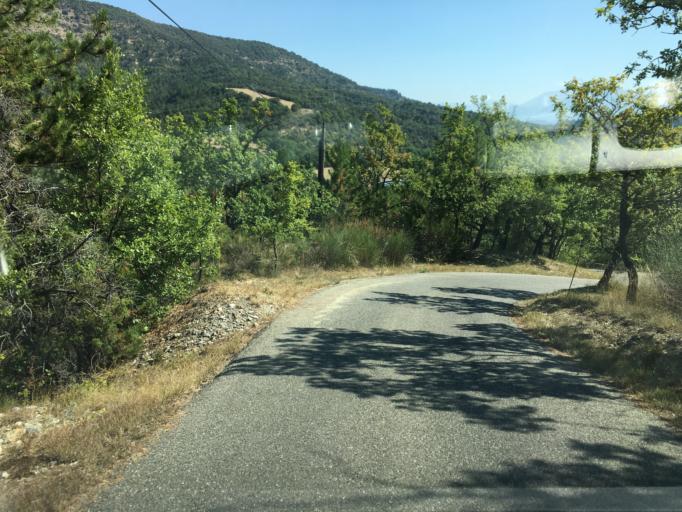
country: FR
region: Provence-Alpes-Cote d'Azur
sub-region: Departement des Alpes-de-Haute-Provence
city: Mallemoisson
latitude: 44.0675
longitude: 6.1321
